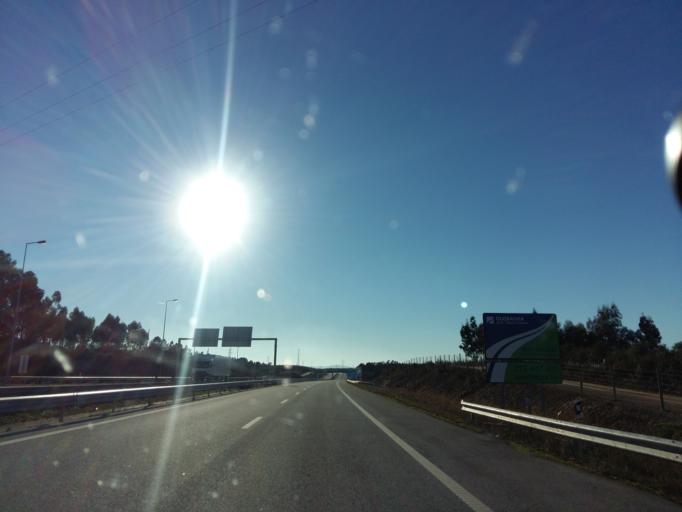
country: PT
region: Castelo Branco
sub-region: Castelo Branco
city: Castelo Branco
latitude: 39.7842
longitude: -7.5731
